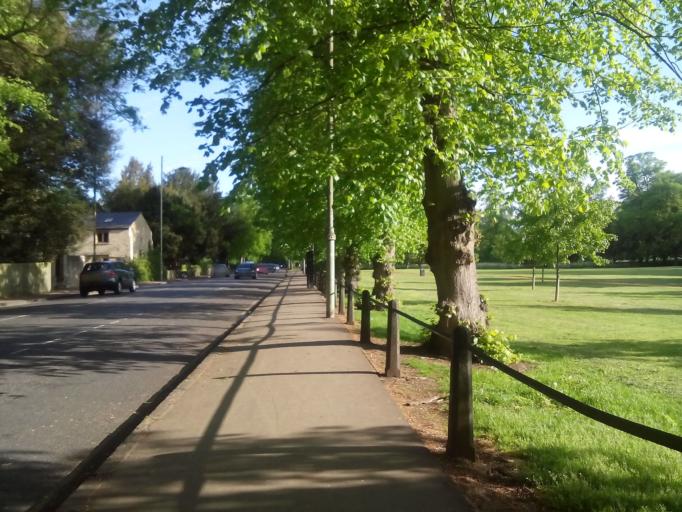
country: GB
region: England
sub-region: Cambridgeshire
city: Cambridge
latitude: 52.2017
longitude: 0.1127
